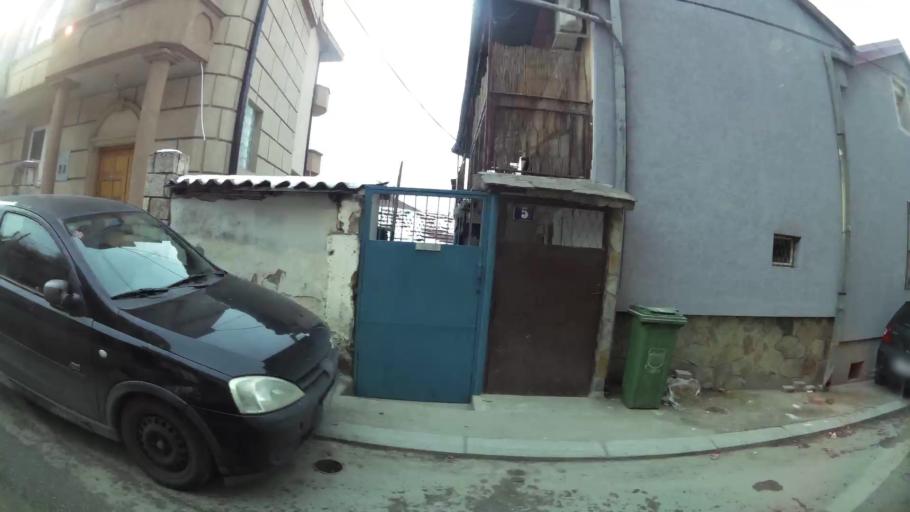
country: MK
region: Cair
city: Cair
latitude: 42.0111
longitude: 21.4465
